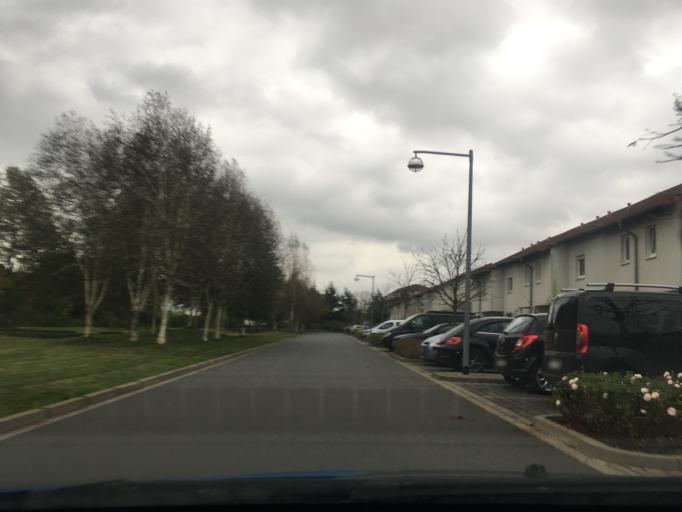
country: DE
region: Lower Saxony
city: Langenhagen
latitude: 52.4810
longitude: 9.7292
